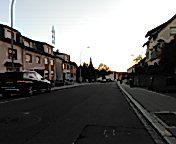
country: LU
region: Luxembourg
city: Belvaux
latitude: 49.5156
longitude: 5.9349
